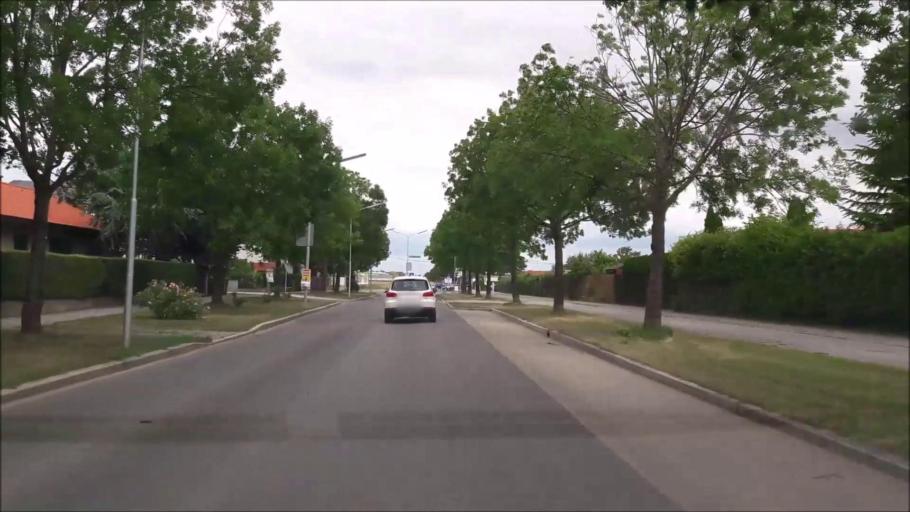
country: AT
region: Lower Austria
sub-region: Politischer Bezirk Wien-Umgebung
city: Gerasdorf bei Wien
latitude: 48.2262
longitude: 16.4842
